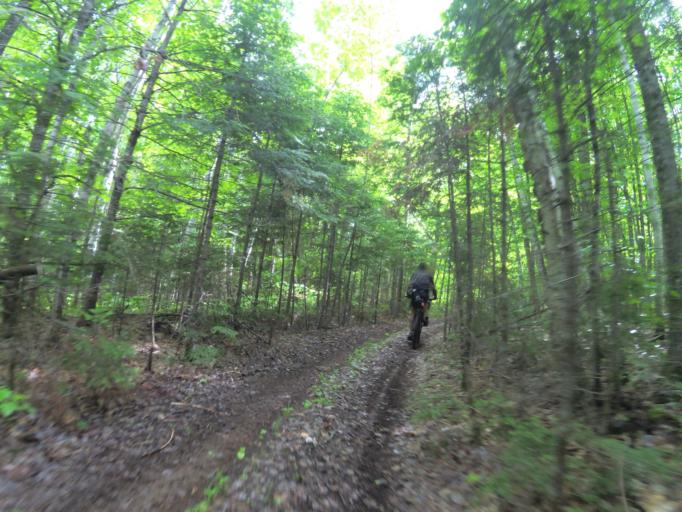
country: CA
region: Ontario
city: Renfrew
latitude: 45.1141
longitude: -76.8533
